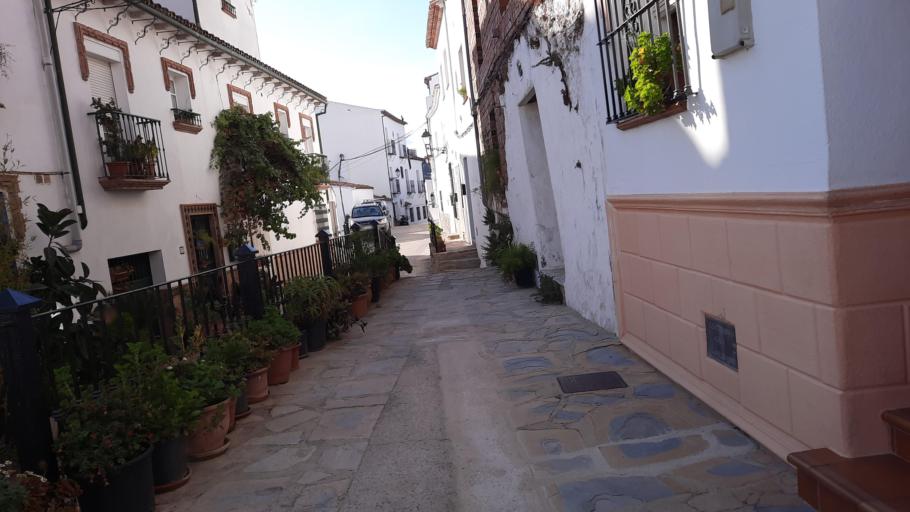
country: ES
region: Andalusia
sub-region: Provincia de Malaga
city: Gaucin
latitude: 36.5184
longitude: -5.3159
